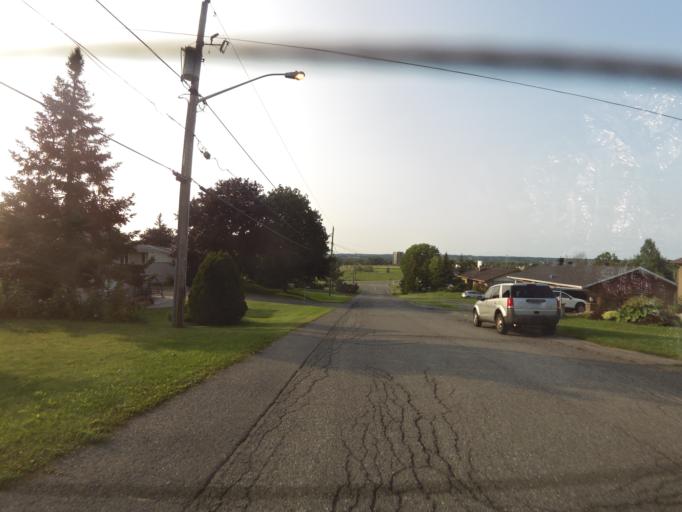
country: CA
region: Ontario
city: Clarence-Rockland
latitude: 45.4889
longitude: -75.4742
